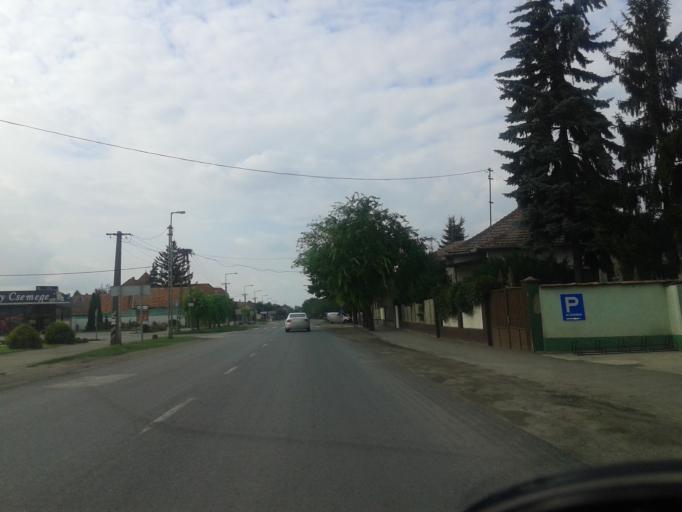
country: HU
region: Bacs-Kiskun
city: Akaszto
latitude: 46.6912
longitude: 19.2052
